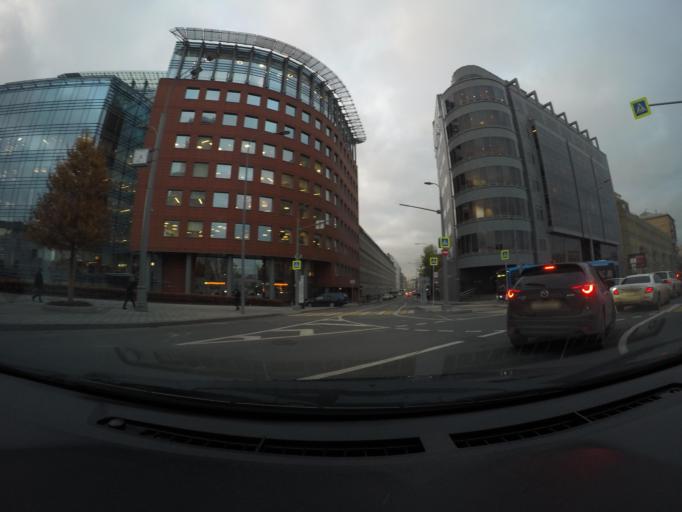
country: RU
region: Moscow
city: Zamoskvorech'ye
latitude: 55.7345
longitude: 37.6431
